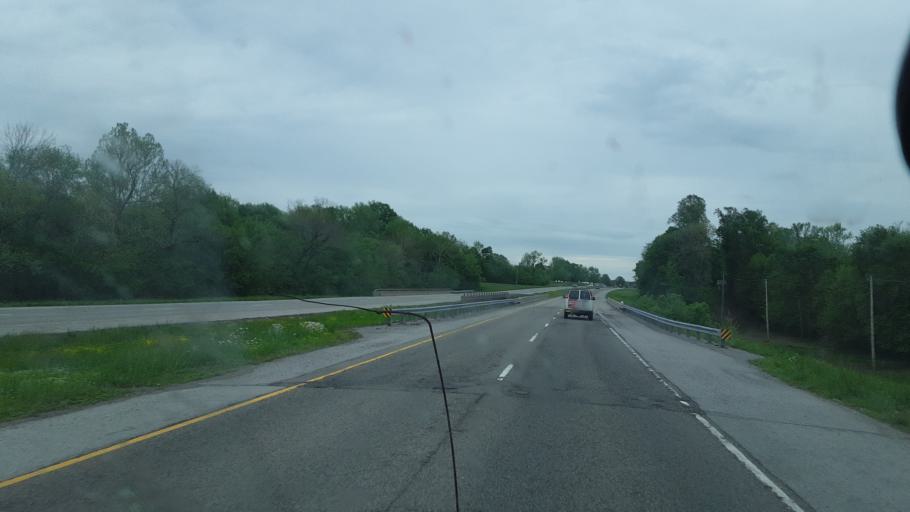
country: US
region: Illinois
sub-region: Jackson County
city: Murphysboro
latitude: 37.7644
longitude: -89.2909
